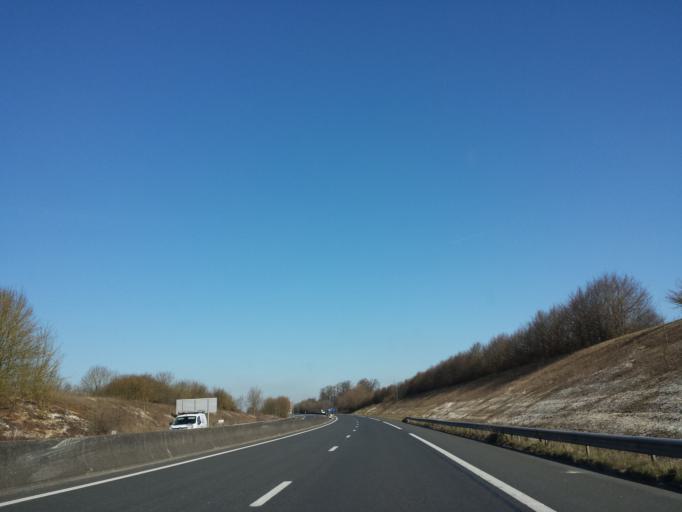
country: FR
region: Picardie
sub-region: Departement de l'Oise
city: Breteuil
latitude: 49.6141
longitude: 2.2087
